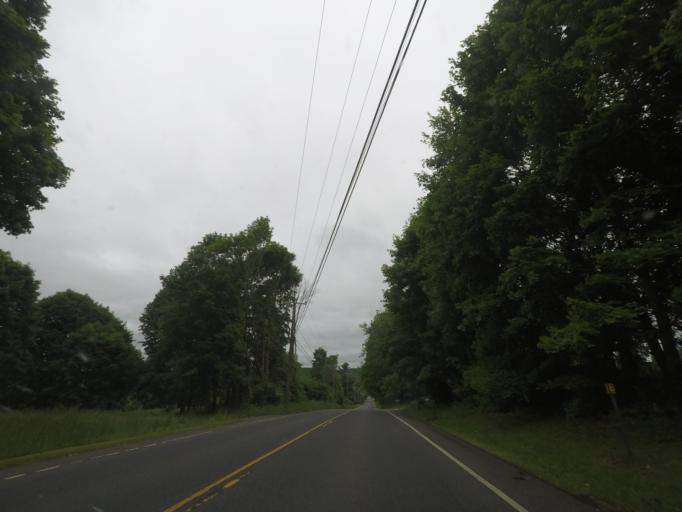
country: US
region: Connecticut
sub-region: Litchfield County
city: Canaan
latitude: 41.9329
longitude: -73.4246
